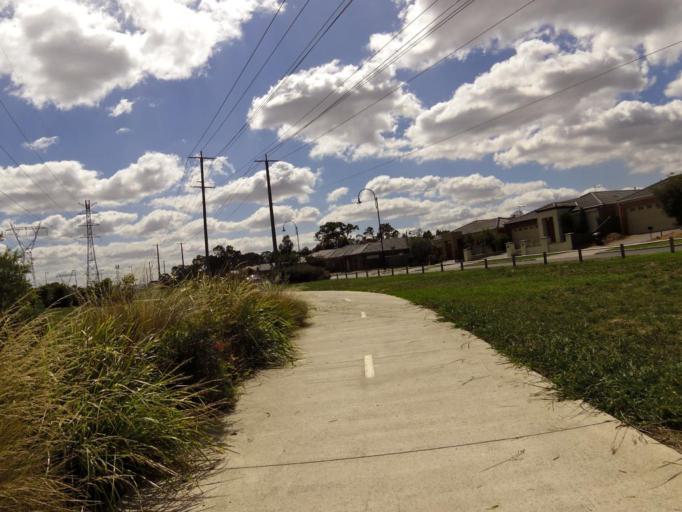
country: AU
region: Victoria
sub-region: Whittlesea
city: Mernda
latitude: -37.6334
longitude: 145.0899
